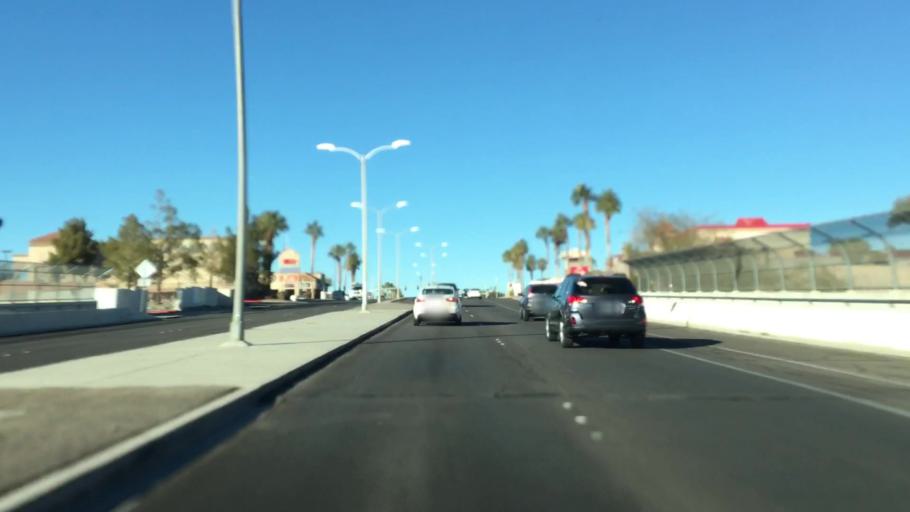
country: US
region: Nevada
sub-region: Clark County
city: Whitney
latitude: 36.0398
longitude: -115.1002
